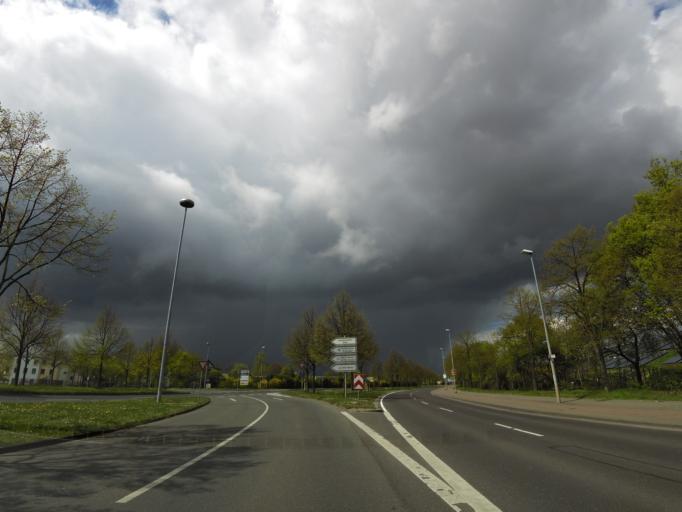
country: DE
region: Saxony-Anhalt
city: Biederitz
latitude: 52.1308
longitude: 11.6791
